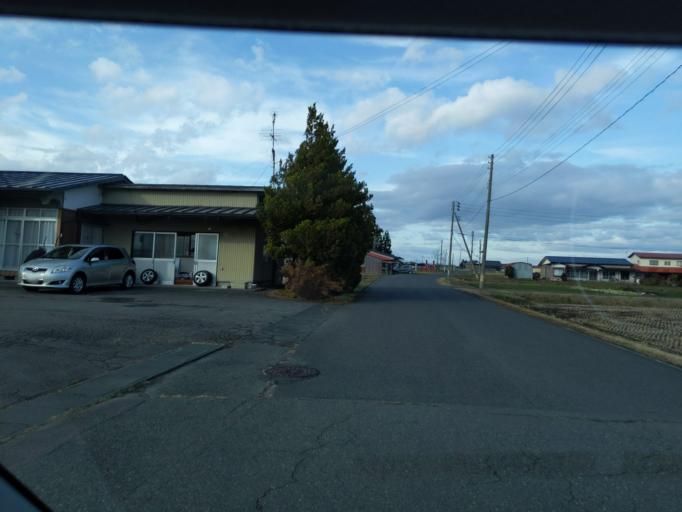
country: JP
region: Iwate
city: Mizusawa
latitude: 39.1484
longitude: 141.0895
